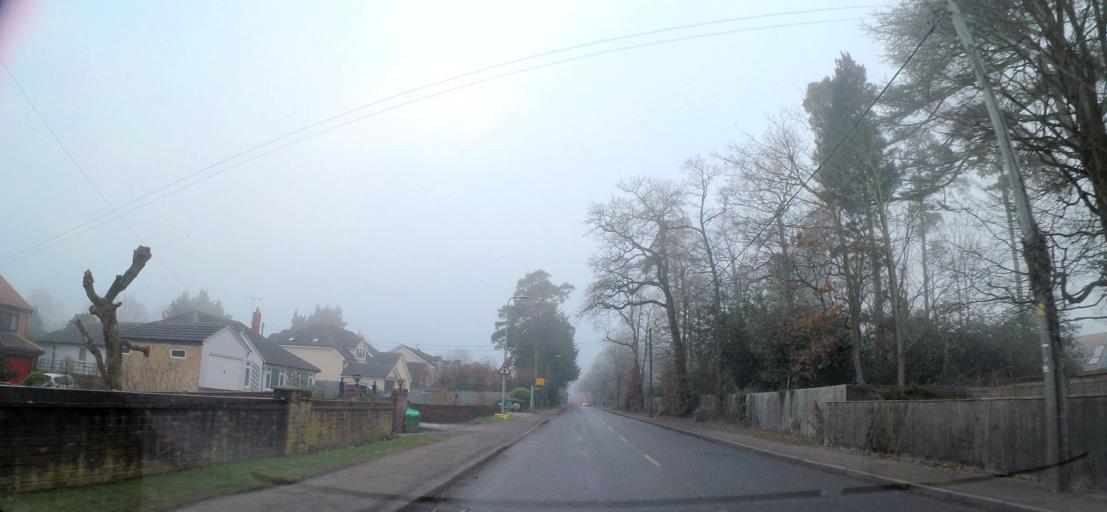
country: GB
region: England
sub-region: West Berkshire
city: Stratfield Mortimer
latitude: 51.3978
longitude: -1.0591
